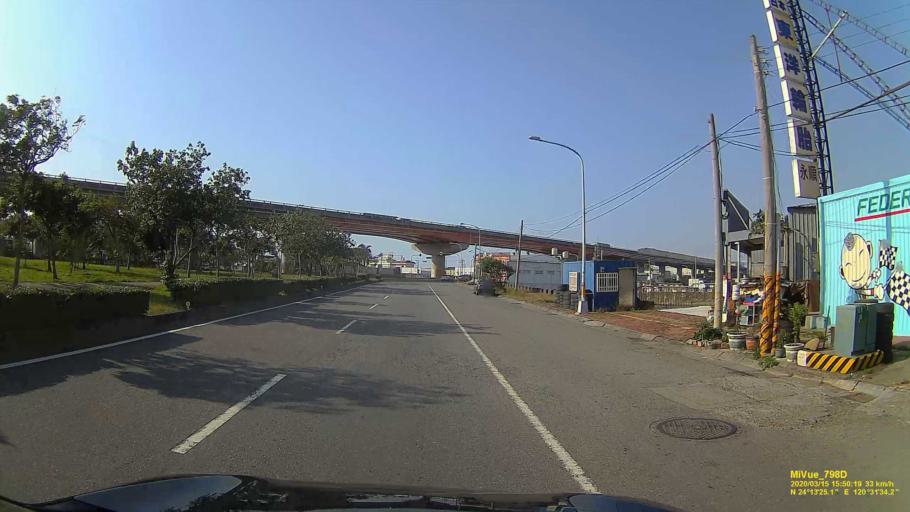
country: TW
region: Taiwan
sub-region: Changhua
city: Chang-hua
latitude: 24.2238
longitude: 120.5262
